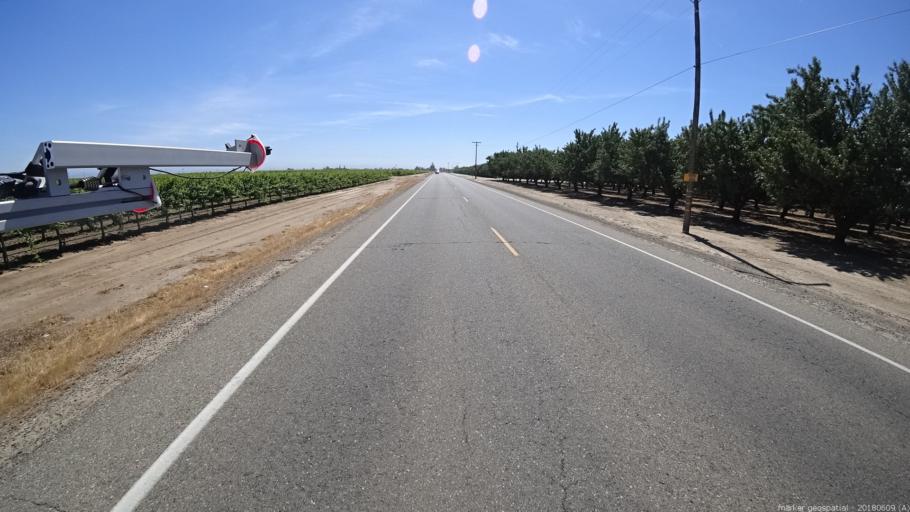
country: US
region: California
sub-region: Madera County
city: Madera
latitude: 36.9529
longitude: -120.1430
